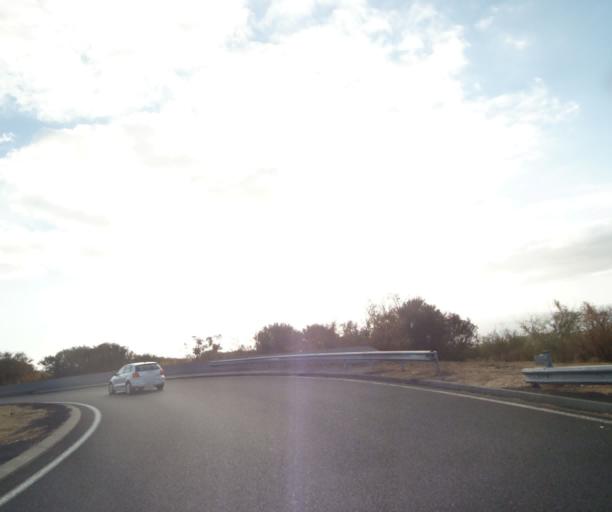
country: RE
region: Reunion
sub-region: Reunion
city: Saint-Paul
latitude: -21.0393
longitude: 55.2498
